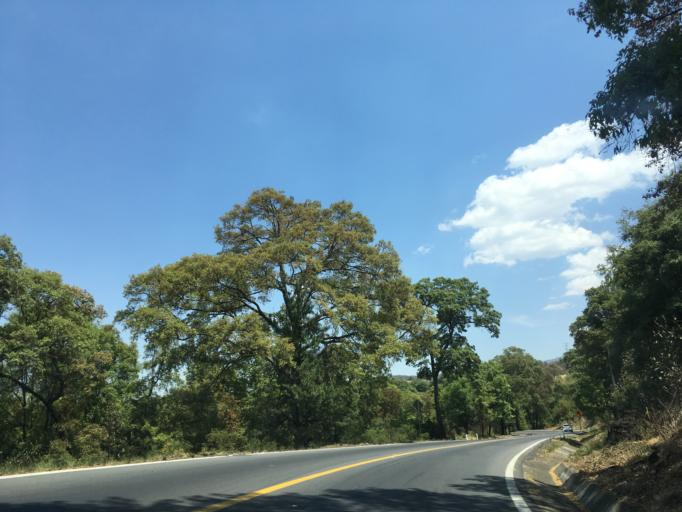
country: MX
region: Michoacan
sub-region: Chilchota
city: Tacuro (Santa Maria Tacuro)
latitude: 19.7973
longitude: -102.0268
